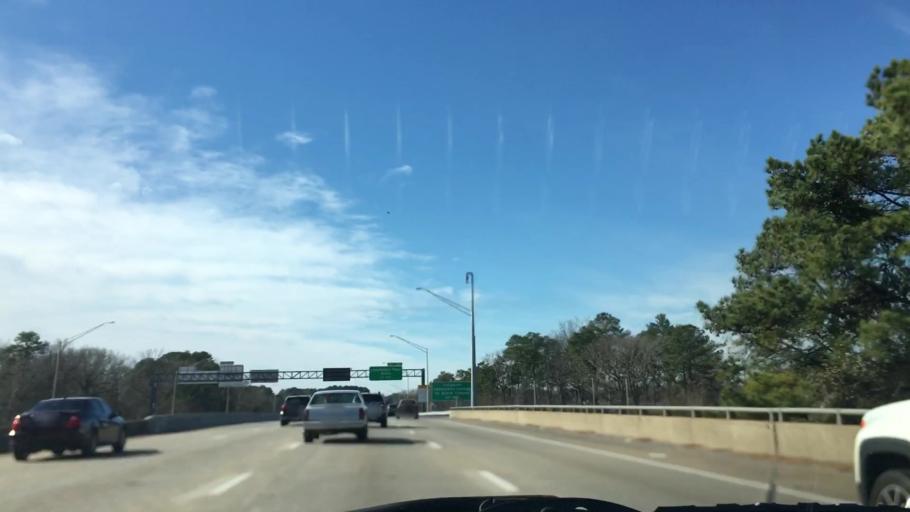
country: US
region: Virginia
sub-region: City of Virginia Beach
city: Virginia Beach
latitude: 36.8392
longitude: -76.0554
